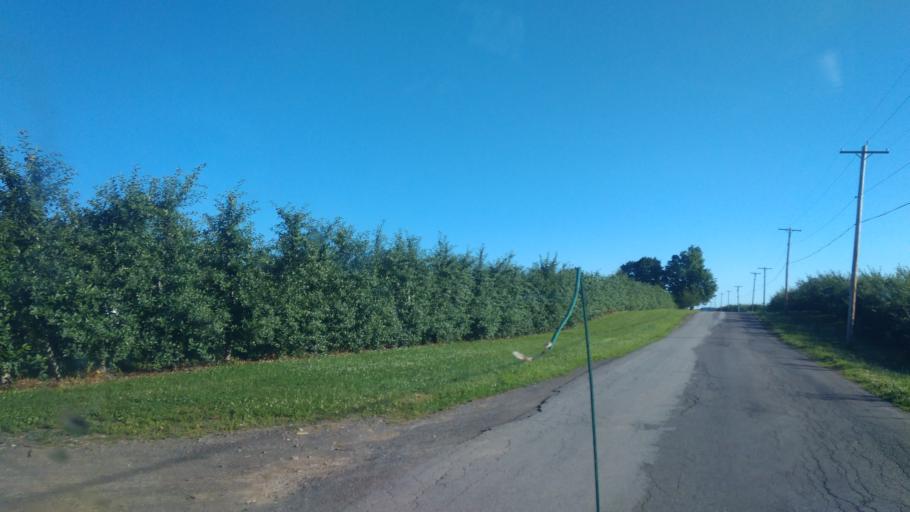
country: US
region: New York
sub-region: Wayne County
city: Sodus
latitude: 43.1766
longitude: -77.0618
